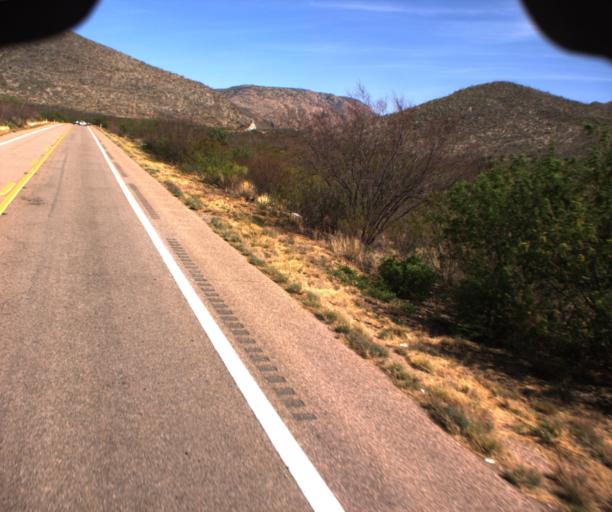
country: US
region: Arizona
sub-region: Cochise County
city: Bisbee
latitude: 31.5216
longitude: -110.0361
